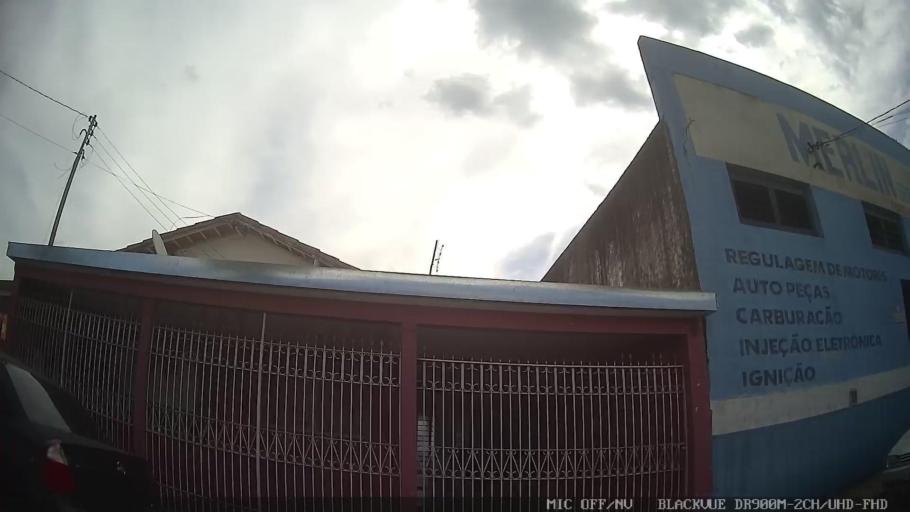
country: BR
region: Sao Paulo
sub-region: Conchas
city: Conchas
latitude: -23.0154
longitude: -48.0039
